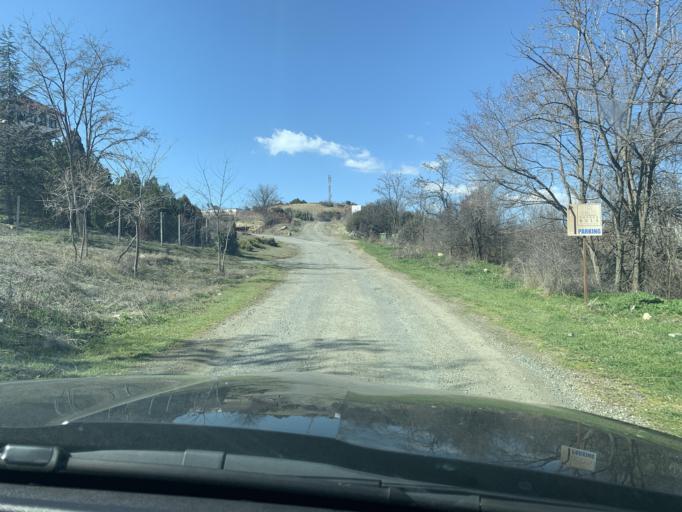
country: MK
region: Demir Kapija
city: Demir Kapija
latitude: 41.4107
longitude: 22.2274
